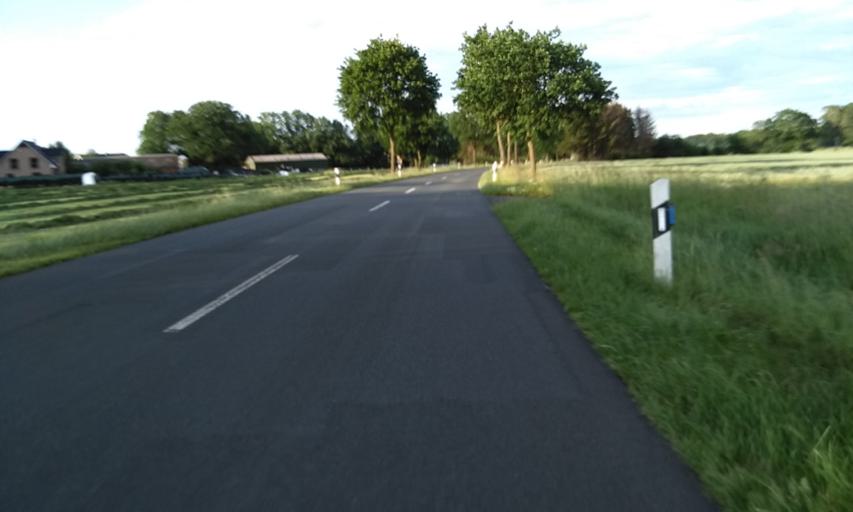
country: DE
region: Lower Saxony
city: Anderlingen
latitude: 53.3848
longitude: 9.3125
